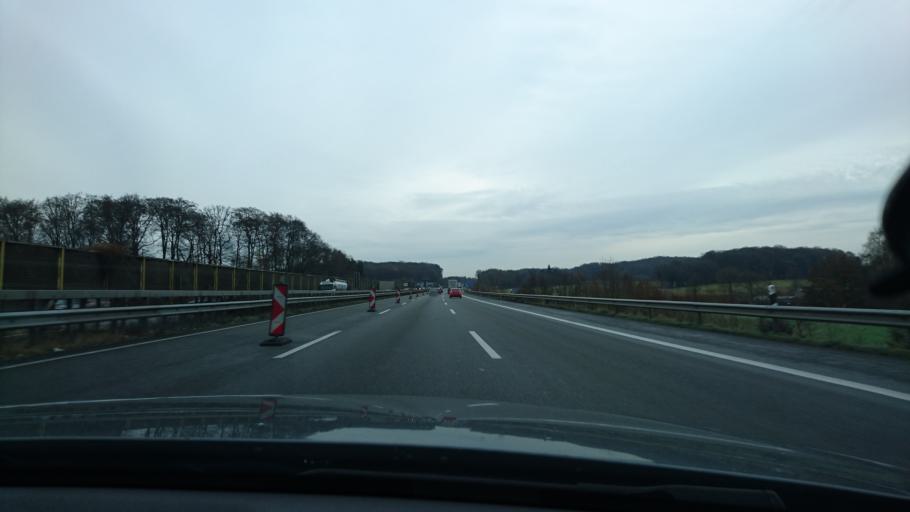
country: DE
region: North Rhine-Westphalia
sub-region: Regierungsbezirk Munster
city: Lotte
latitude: 52.3086
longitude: 7.9480
